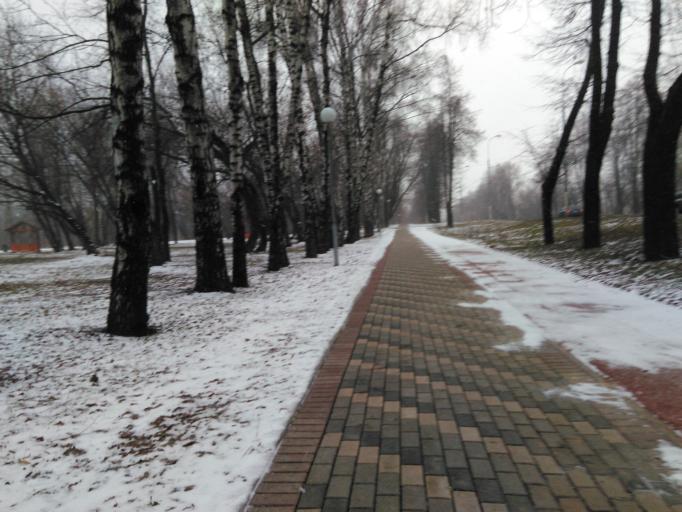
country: RU
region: Moskovskaya
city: Kur'yanovo
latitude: 55.6331
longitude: 37.6951
